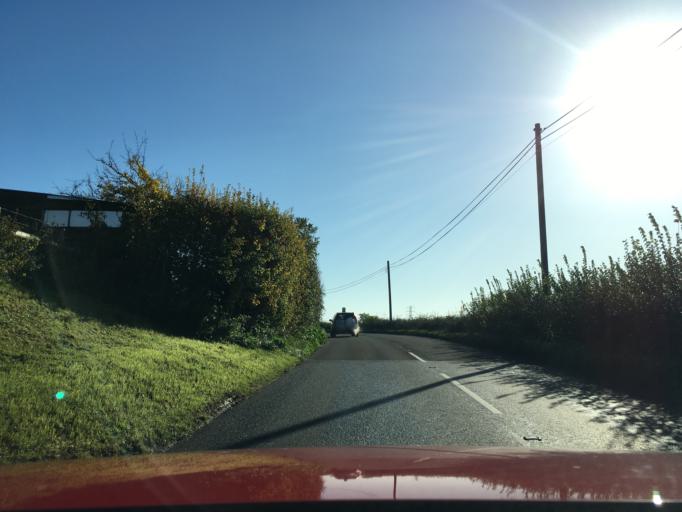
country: GB
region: England
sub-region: Somerset
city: Langport
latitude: 51.0566
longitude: -2.8522
